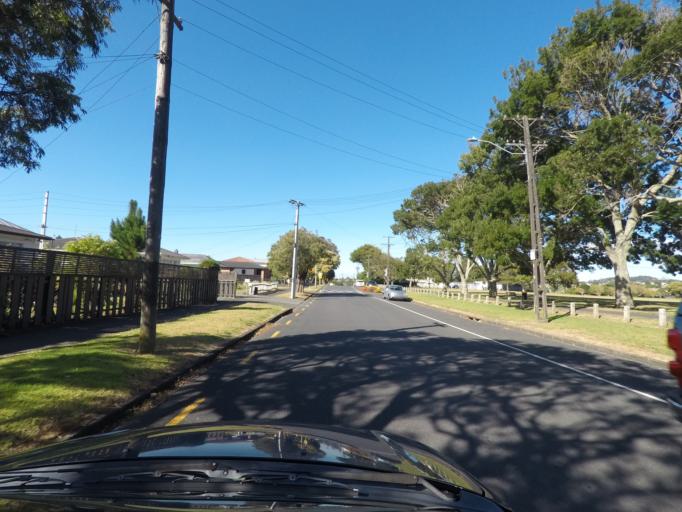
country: NZ
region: Auckland
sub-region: Auckland
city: Rosebank
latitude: -36.8868
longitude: 174.6859
